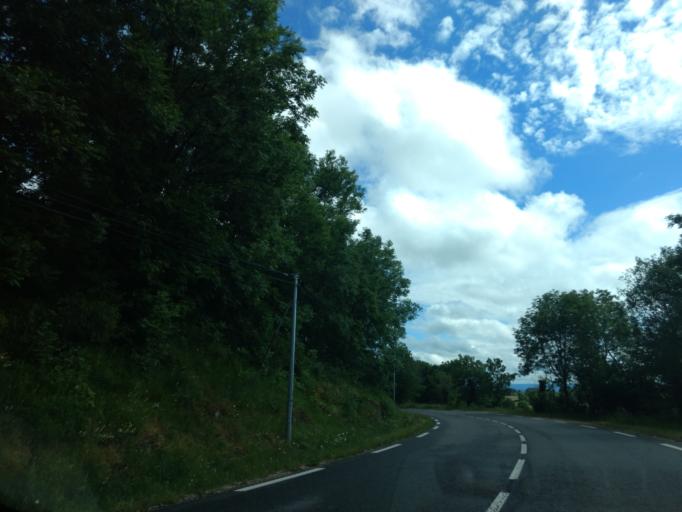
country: FR
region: Midi-Pyrenees
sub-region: Departement de l'Aveyron
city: Laguiole
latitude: 44.6686
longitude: 2.8492
